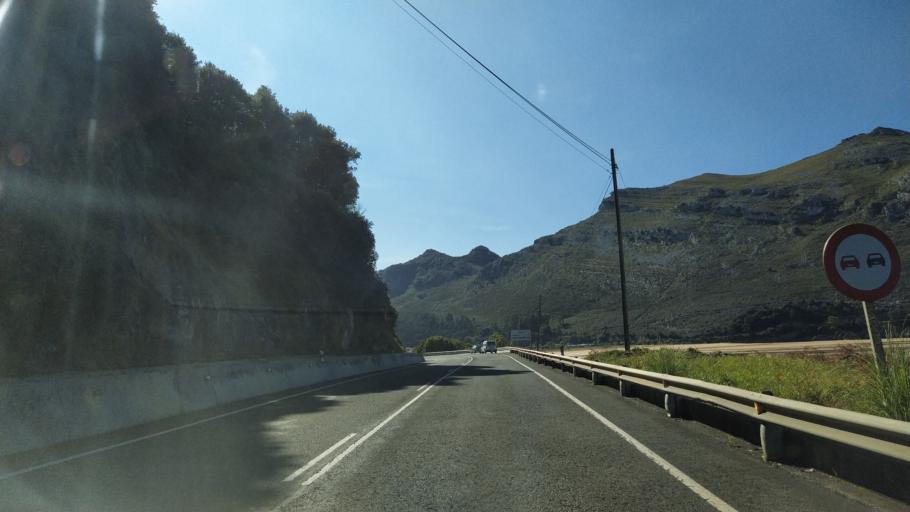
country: ES
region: Cantabria
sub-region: Provincia de Cantabria
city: Liendo
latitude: 43.4026
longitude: -3.3144
